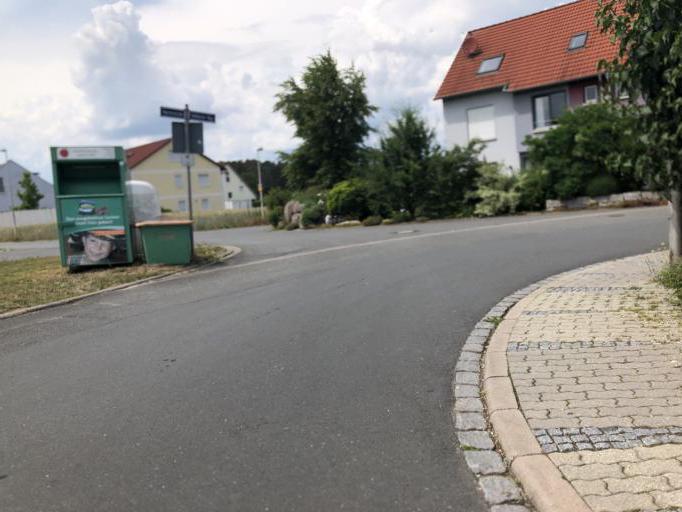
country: DE
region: Bavaria
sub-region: Regierungsbezirk Mittelfranken
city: Hessdorf
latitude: 49.6255
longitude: 10.9347
